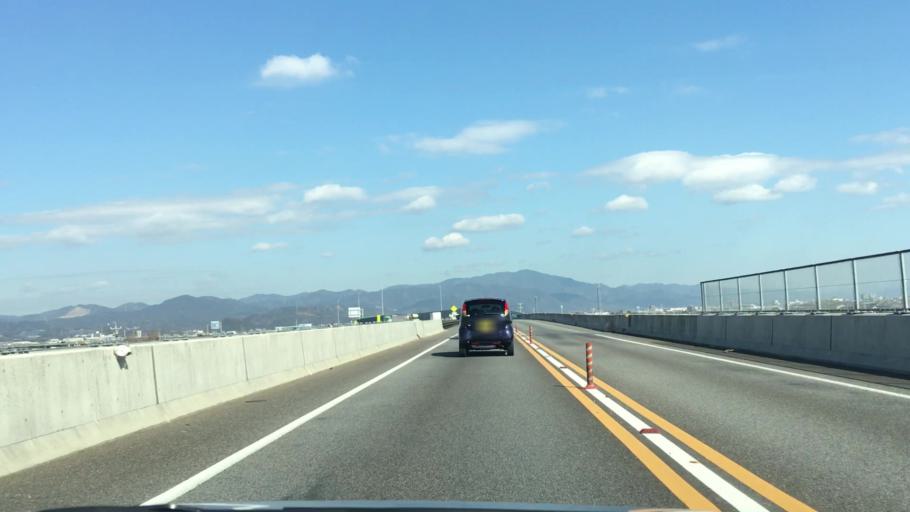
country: JP
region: Aichi
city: Kozakai-cho
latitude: 34.8019
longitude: 137.3358
